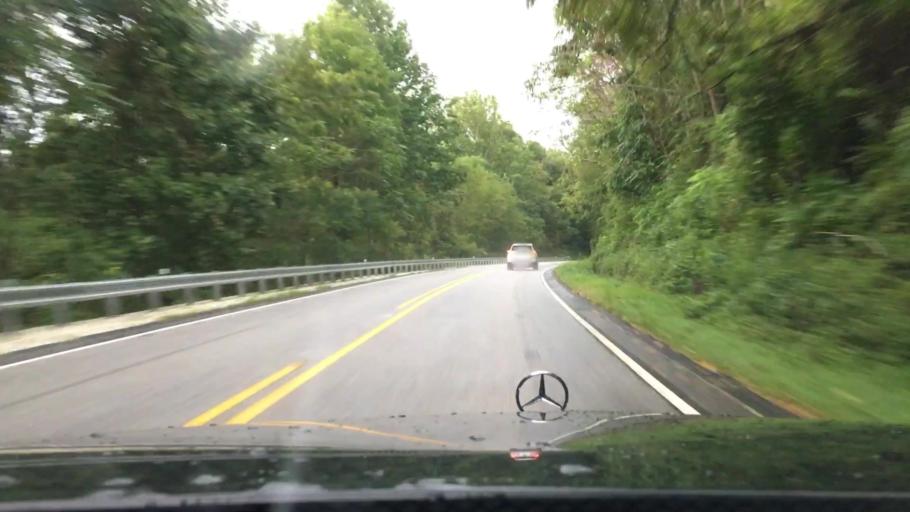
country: US
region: Virginia
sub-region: Amherst County
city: Amherst
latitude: 37.6757
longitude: -79.0161
